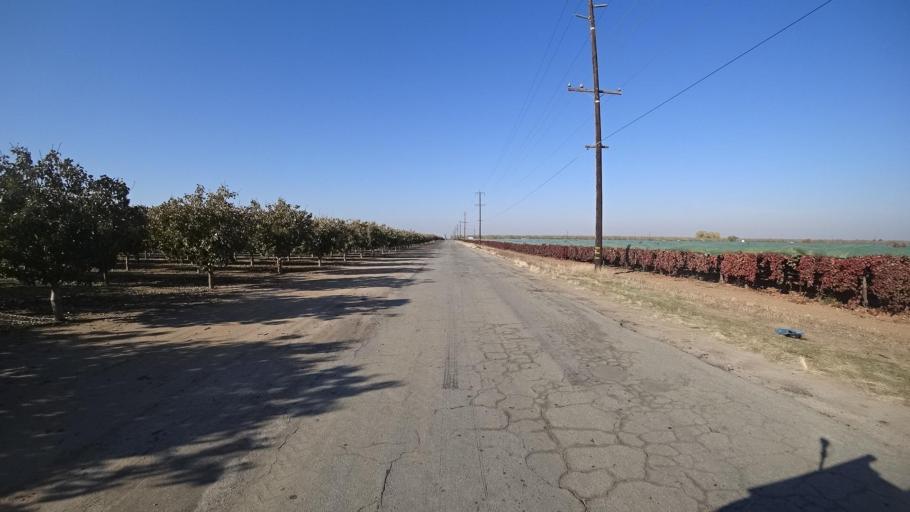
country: US
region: California
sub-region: Tulare County
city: Richgrove
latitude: 35.7327
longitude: -119.1211
